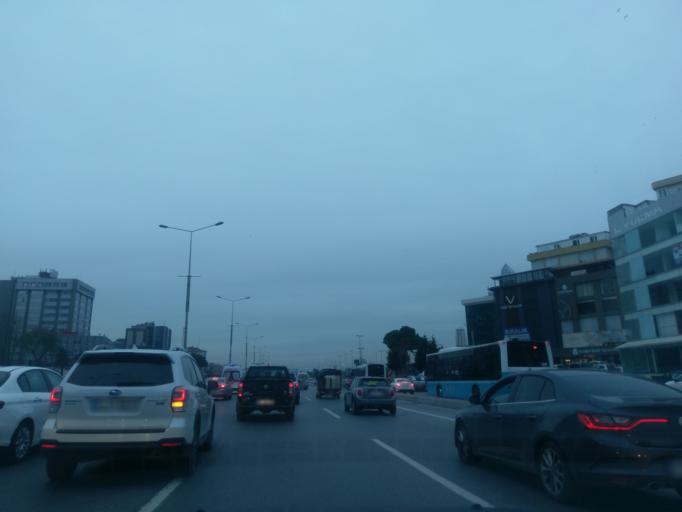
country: TR
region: Istanbul
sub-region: Atasehir
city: Atasehir
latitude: 40.9733
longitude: 29.1002
